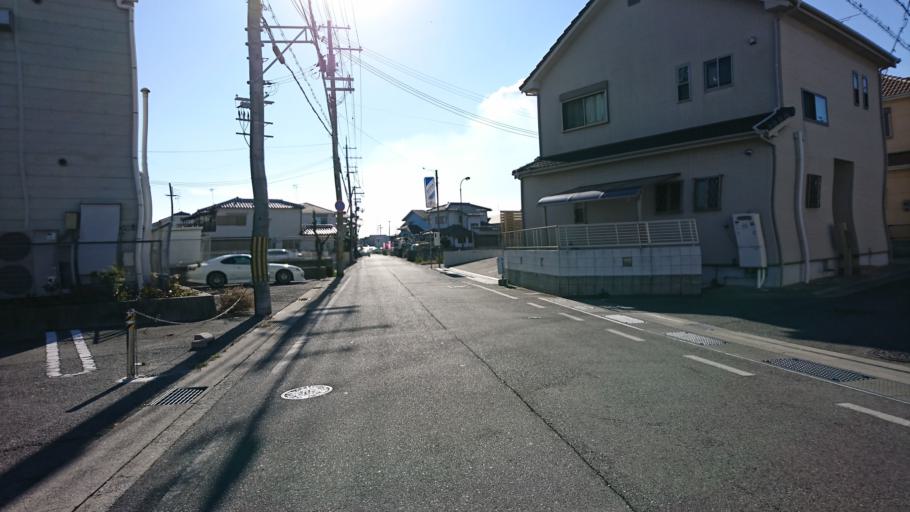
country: JP
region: Hyogo
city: Kakogawacho-honmachi
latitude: 34.7443
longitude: 134.8389
